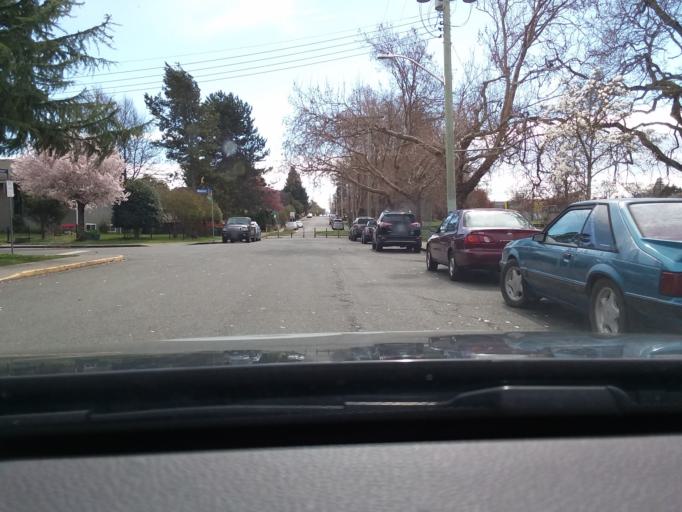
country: CA
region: British Columbia
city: Victoria
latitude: 48.4342
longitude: -123.3494
